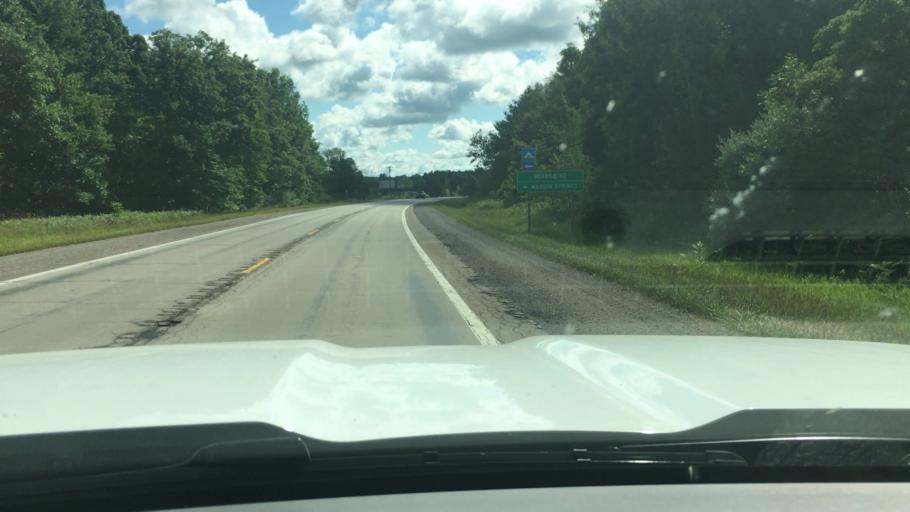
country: US
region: Michigan
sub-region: Clinton County
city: Ovid
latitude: 43.1861
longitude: -84.3293
